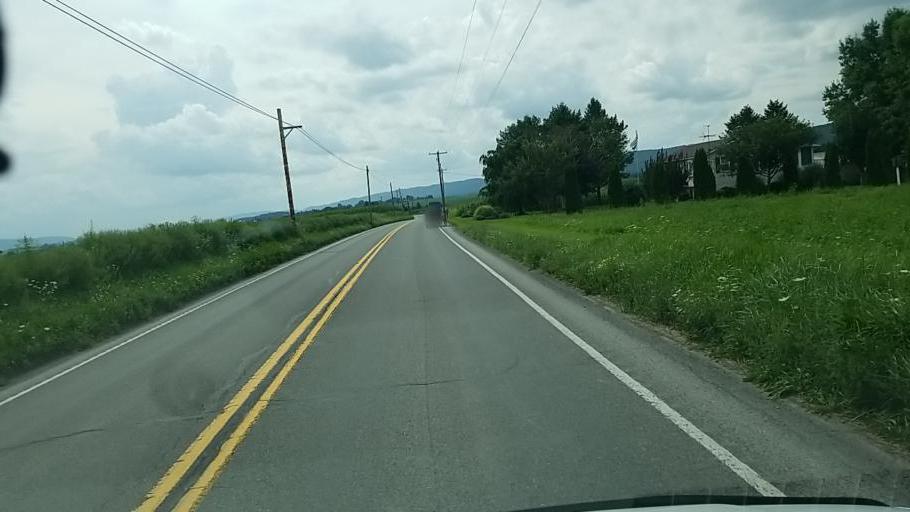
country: US
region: Pennsylvania
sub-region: Dauphin County
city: Elizabethville
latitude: 40.6061
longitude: -76.7835
